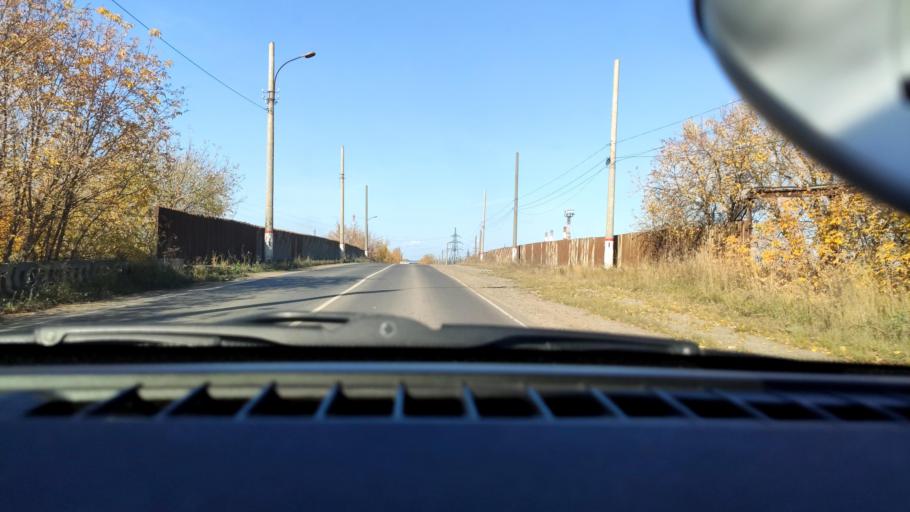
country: RU
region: Perm
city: Gamovo
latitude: 57.9097
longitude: 56.1625
